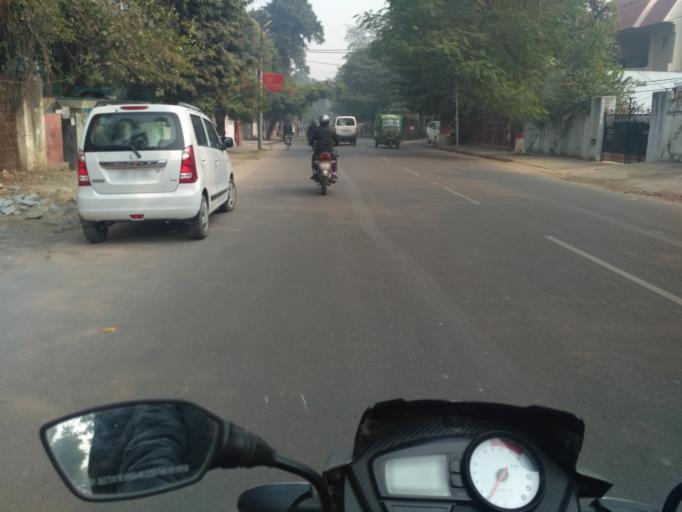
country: IN
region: Uttar Pradesh
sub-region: Kanpur
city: Nawabganj
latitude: 26.4866
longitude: 80.3189
